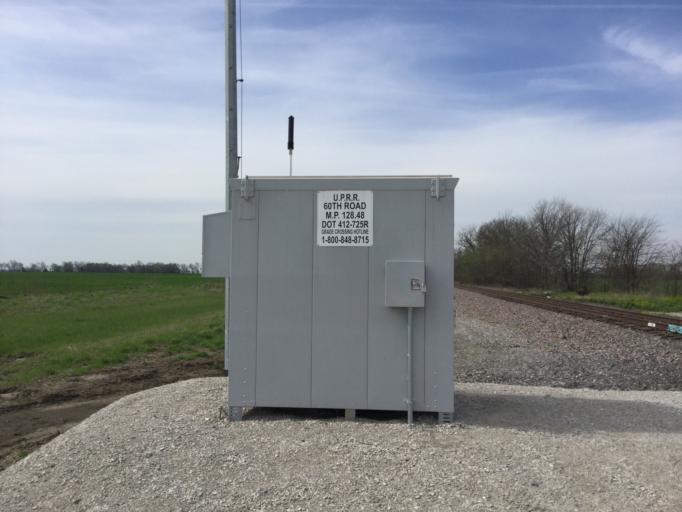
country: US
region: Kansas
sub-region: Neosho County
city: Erie
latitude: 37.4567
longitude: -95.2545
